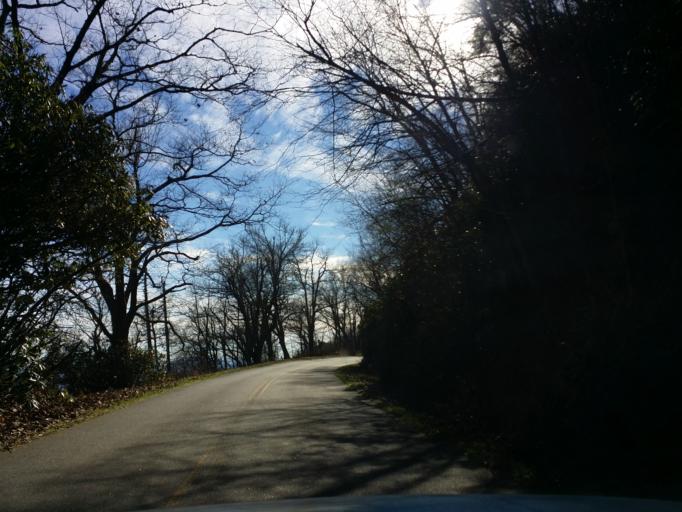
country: US
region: North Carolina
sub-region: Buncombe County
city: Black Mountain
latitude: 35.7213
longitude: -82.2207
